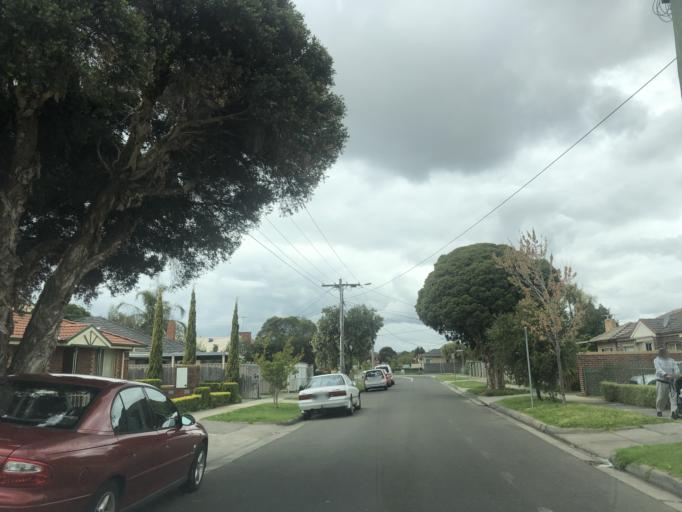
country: AU
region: Victoria
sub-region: Greater Dandenong
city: Dandenong North
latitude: -37.9754
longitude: 145.2120
